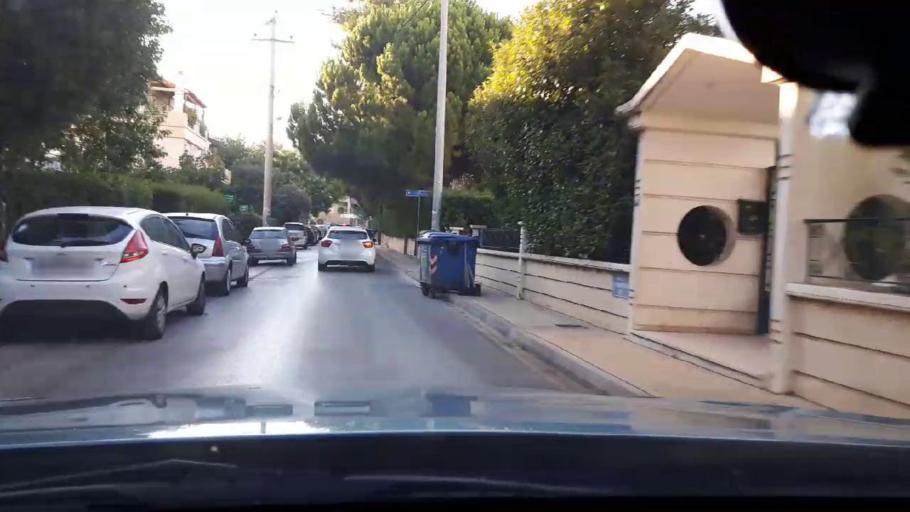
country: GR
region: Attica
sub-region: Nomarchia Athinas
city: Melissia
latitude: 38.0505
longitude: 23.8321
